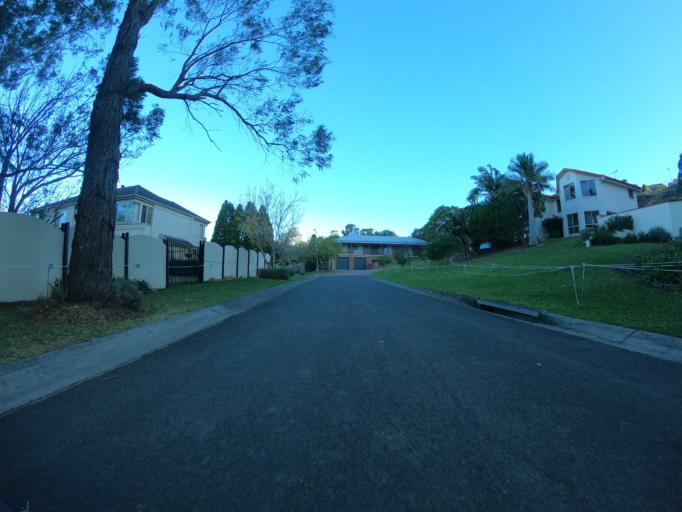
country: AU
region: New South Wales
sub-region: Wollongong
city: Mount Keira
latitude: -34.4230
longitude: 150.8457
